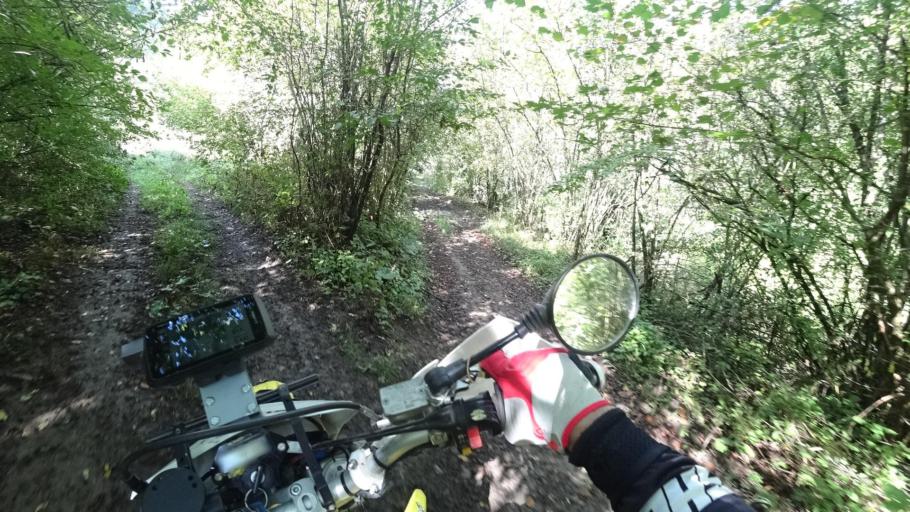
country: BA
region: Republika Srpska
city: Hiseti
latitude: 44.7688
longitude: 17.1367
